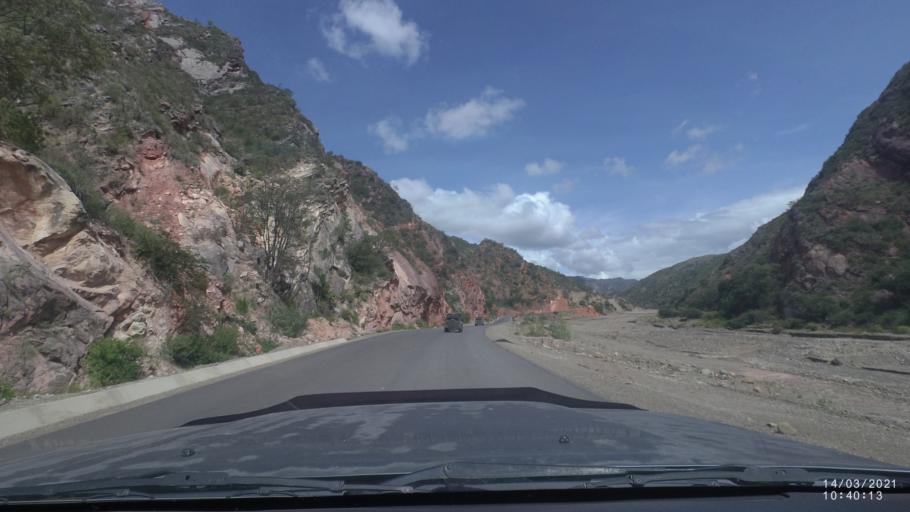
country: BO
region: Cochabamba
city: Cliza
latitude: -17.8824
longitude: -65.9015
